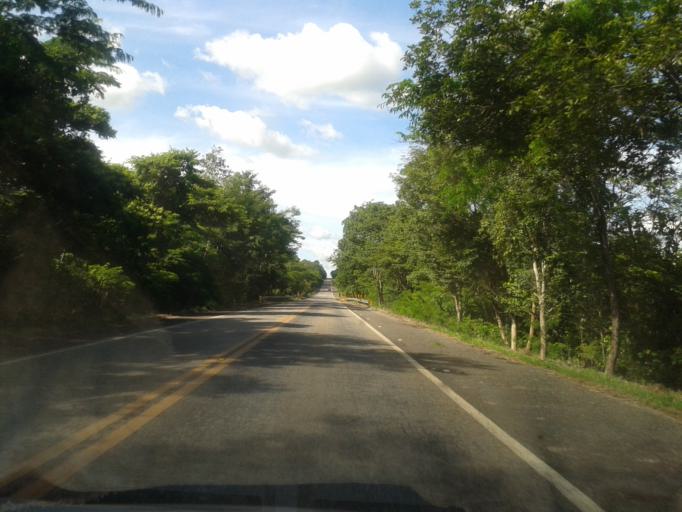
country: BR
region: Goias
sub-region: Mozarlandia
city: Mozarlandia
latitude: -14.9831
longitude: -50.5812
